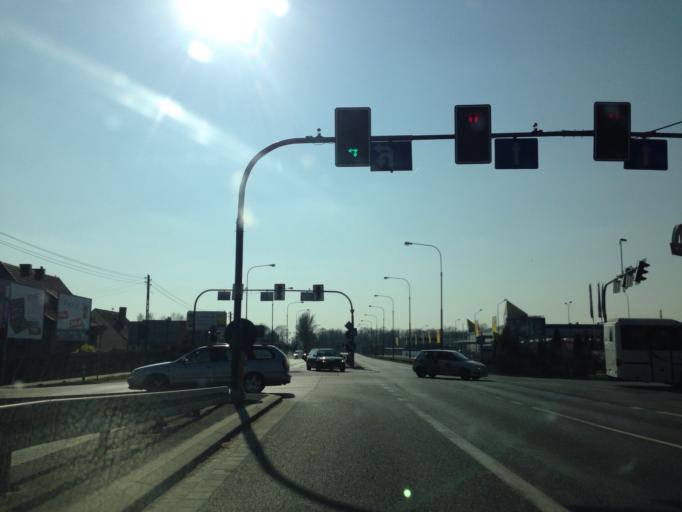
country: PL
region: Lower Silesian Voivodeship
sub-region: Powiat wroclawski
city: Dlugoleka
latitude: 51.1810
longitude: 17.2007
